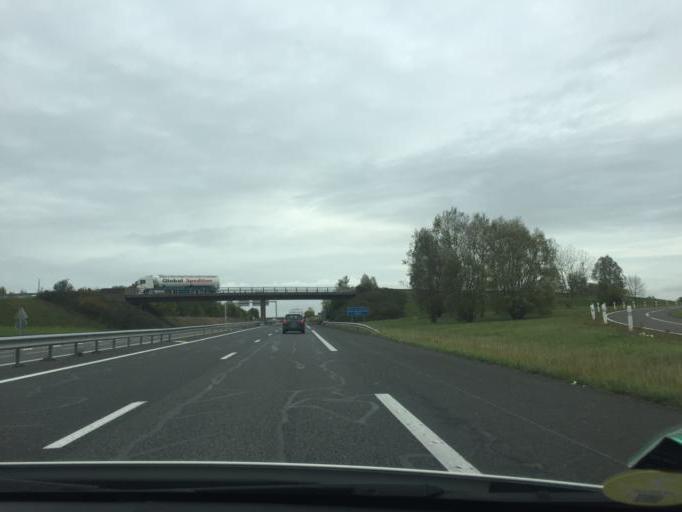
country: FR
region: Bourgogne
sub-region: Departement de l'Yonne
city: Egriselles-le-Bocage
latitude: 48.1473
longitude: 3.1644
